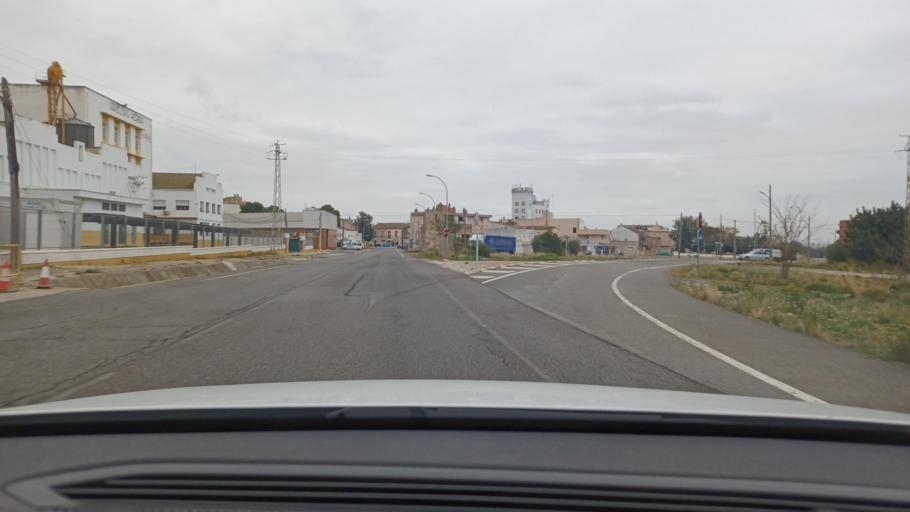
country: ES
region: Catalonia
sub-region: Provincia de Tarragona
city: Camarles
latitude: 40.7490
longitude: 0.6200
